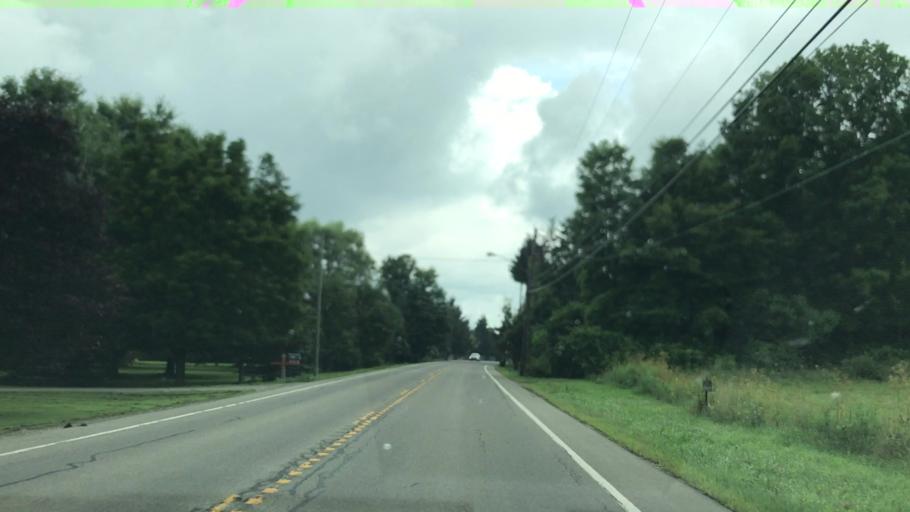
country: US
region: New York
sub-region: Steuben County
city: Bath
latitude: 42.3820
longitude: -77.3603
